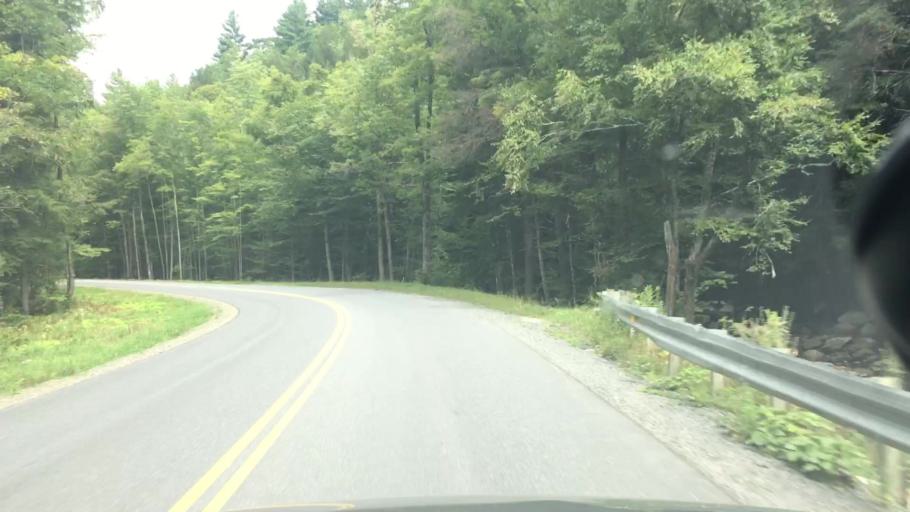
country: US
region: Massachusetts
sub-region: Franklin County
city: Colrain
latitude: 42.7615
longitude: -72.7618
